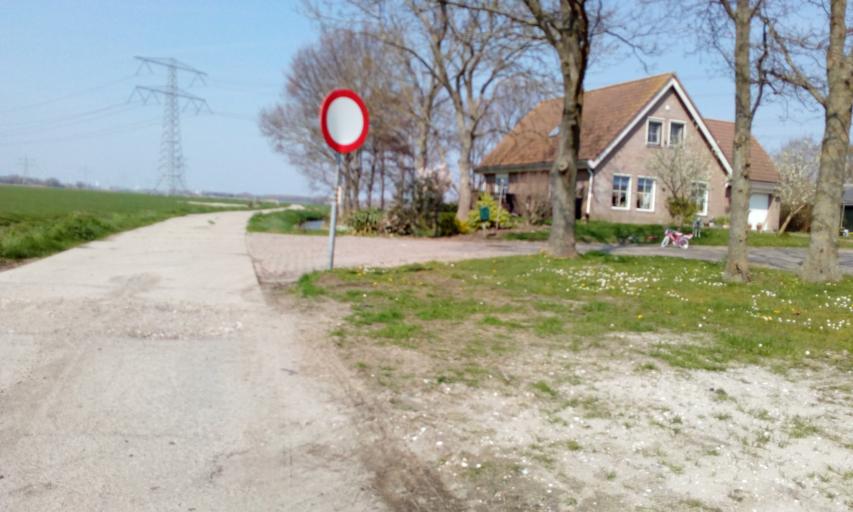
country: NL
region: South Holland
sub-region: Gemeente Spijkenisse
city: Spijkenisse
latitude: 51.8225
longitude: 4.3099
